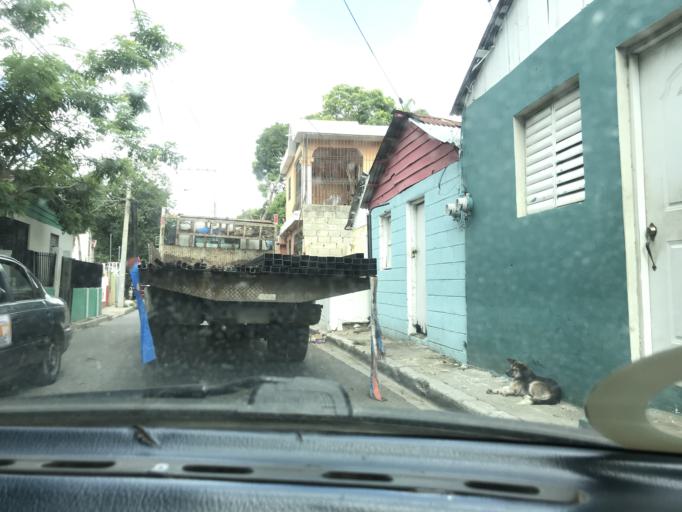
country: DO
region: Santiago
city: Santiago de los Caballeros
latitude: 19.4527
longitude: -70.7287
